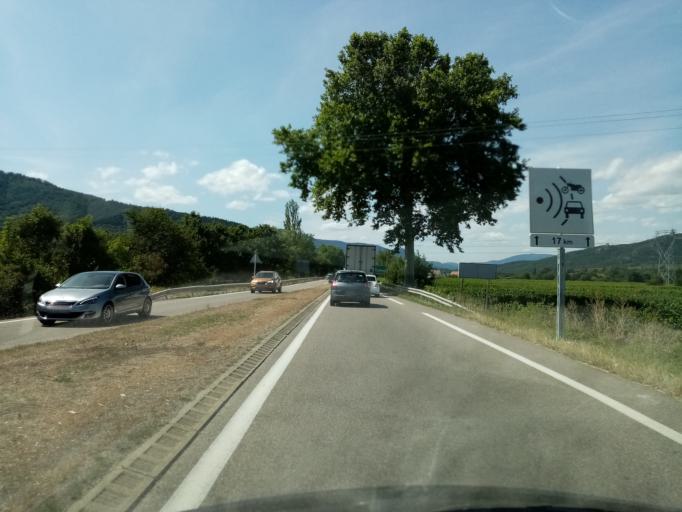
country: FR
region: Alsace
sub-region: Departement du Bas-Rhin
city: Scherwiller
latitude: 48.2716
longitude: 7.4160
